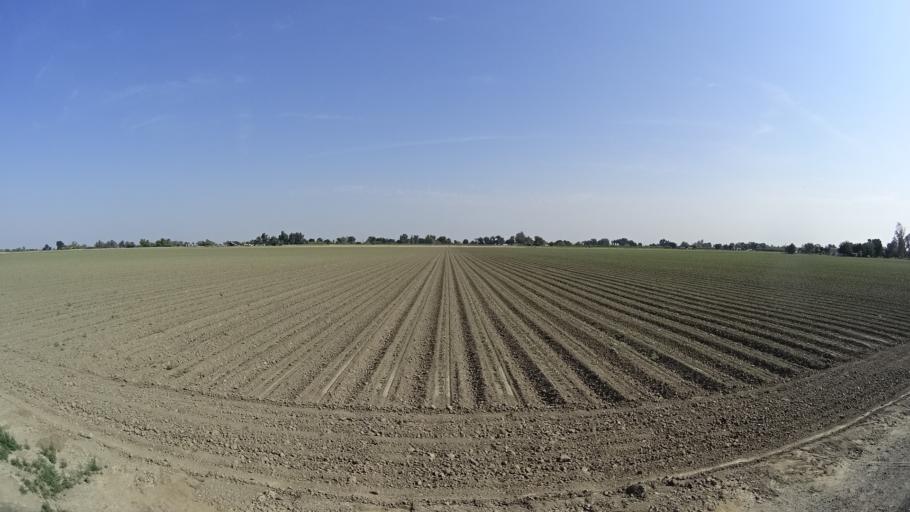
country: US
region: California
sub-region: Kings County
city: Lemoore
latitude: 36.3366
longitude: -119.8569
